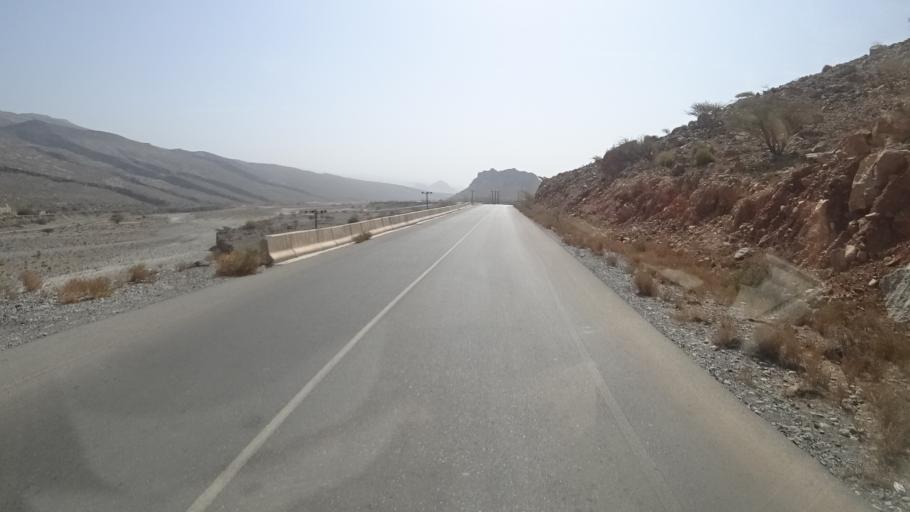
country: OM
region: Muhafazat ad Dakhiliyah
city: Bahla'
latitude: 23.1426
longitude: 57.2168
